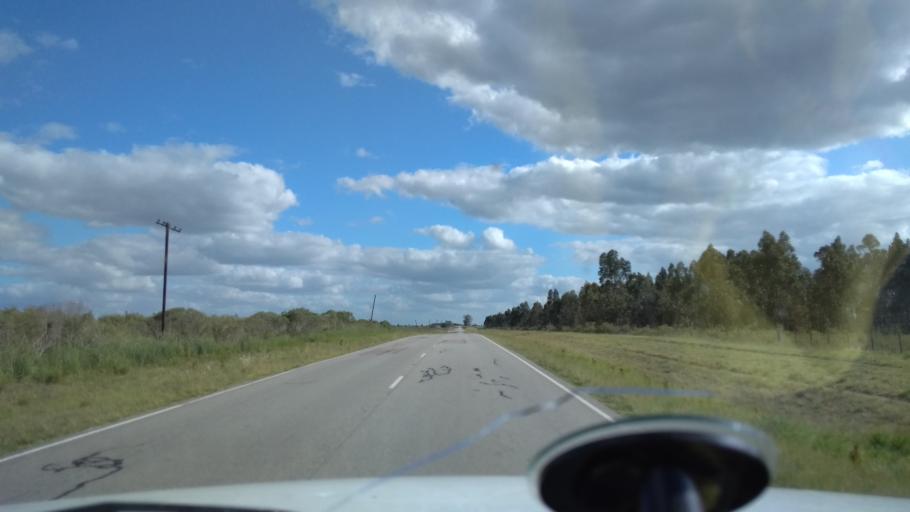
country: UY
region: Florida
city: Casupa
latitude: -34.1317
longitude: -55.6744
